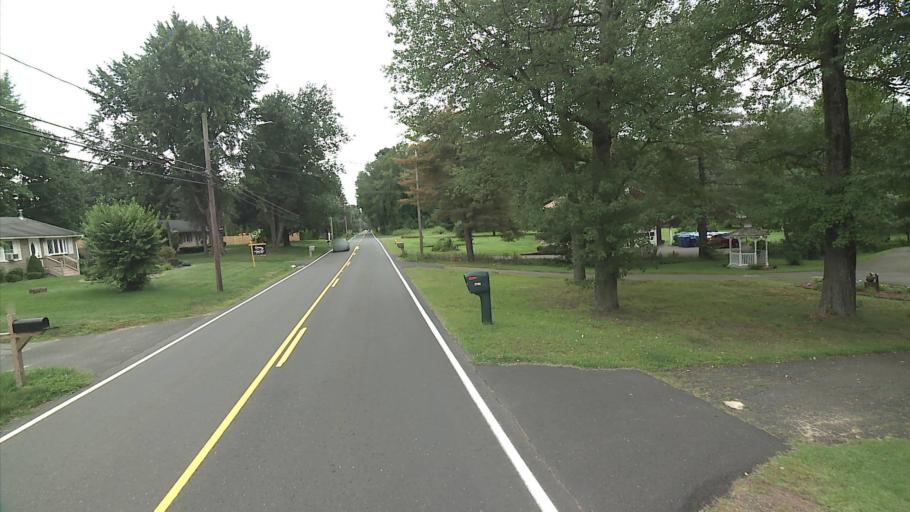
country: US
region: Connecticut
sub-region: Hartford County
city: Broad Brook
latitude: 41.8506
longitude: -72.5223
